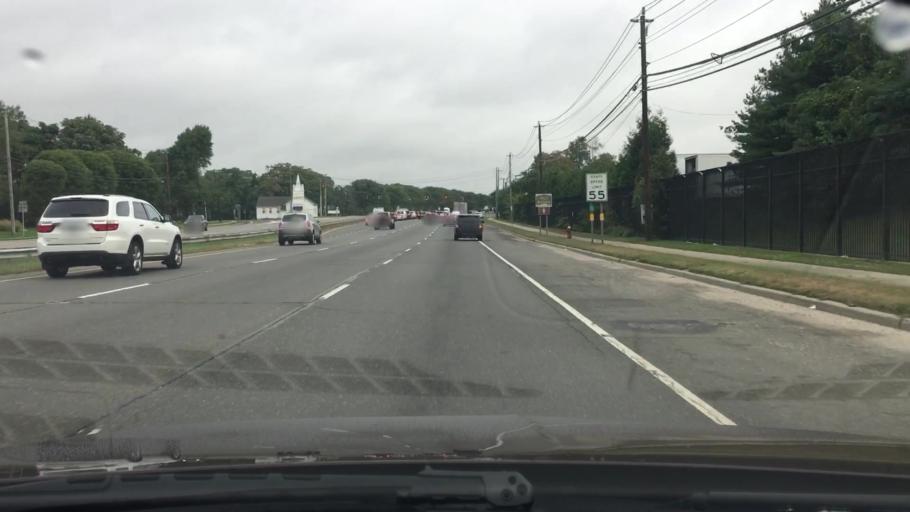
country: US
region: New York
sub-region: Suffolk County
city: Melville
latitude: 40.7646
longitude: -73.4233
